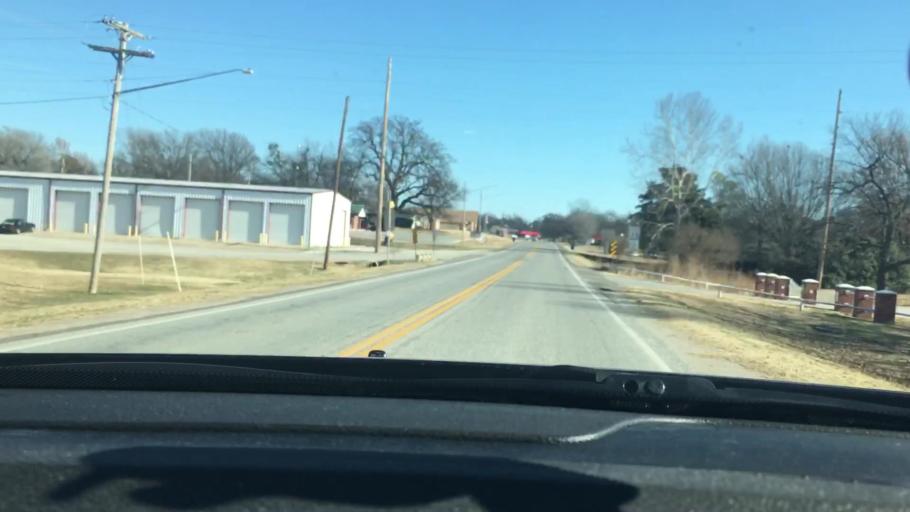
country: US
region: Oklahoma
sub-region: Garvin County
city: Wynnewood
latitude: 34.6438
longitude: -97.1625
